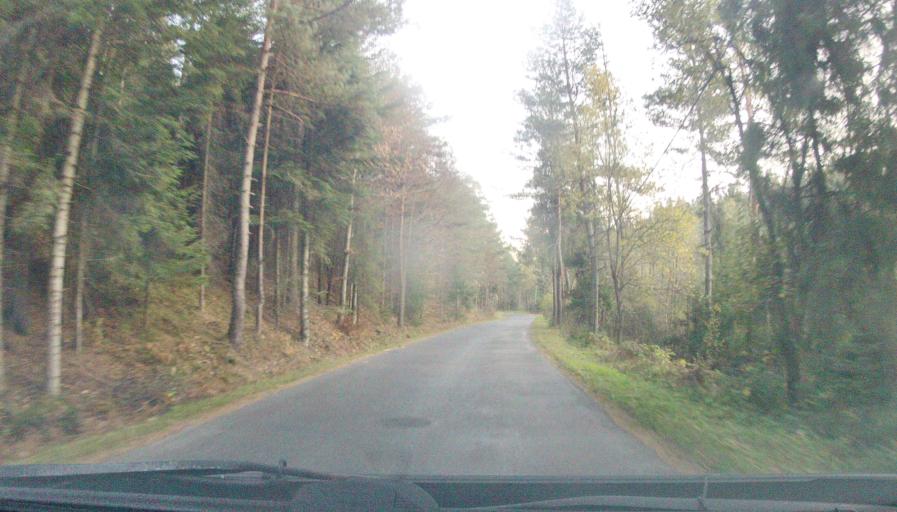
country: PL
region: Lesser Poland Voivodeship
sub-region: Powiat suski
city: Krzeszow
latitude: 49.7536
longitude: 19.4606
